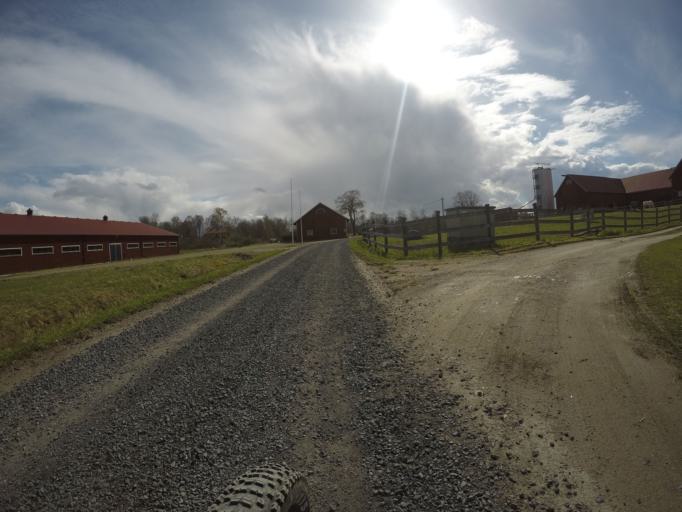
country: SE
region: Vaestmanland
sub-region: Kungsors Kommun
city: Kungsoer
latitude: 59.2808
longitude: 16.1530
